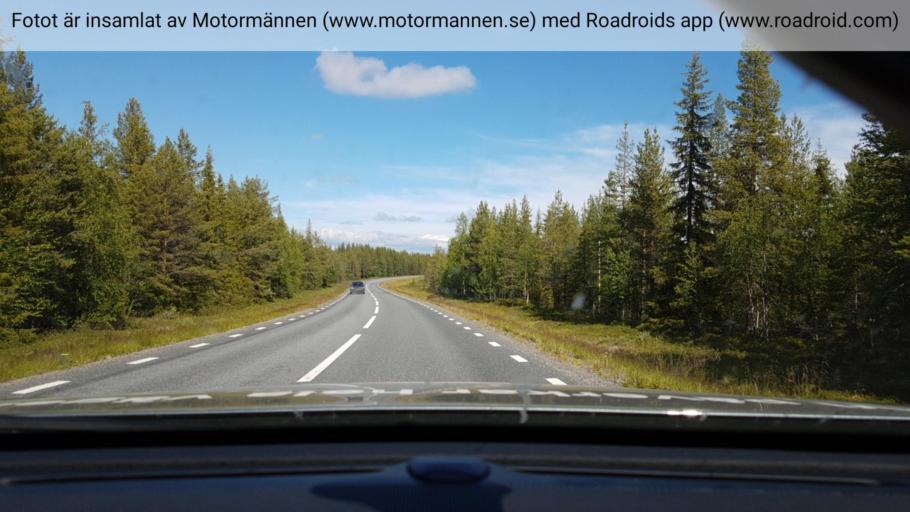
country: SE
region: Vaesterbotten
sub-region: Sorsele Kommun
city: Sorsele
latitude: 65.5614
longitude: 17.9693
